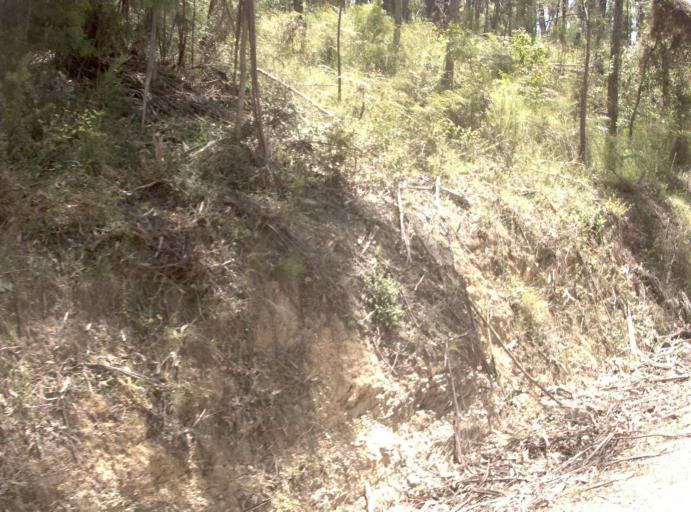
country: AU
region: New South Wales
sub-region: Bombala
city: Bombala
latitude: -37.5767
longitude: 148.9391
